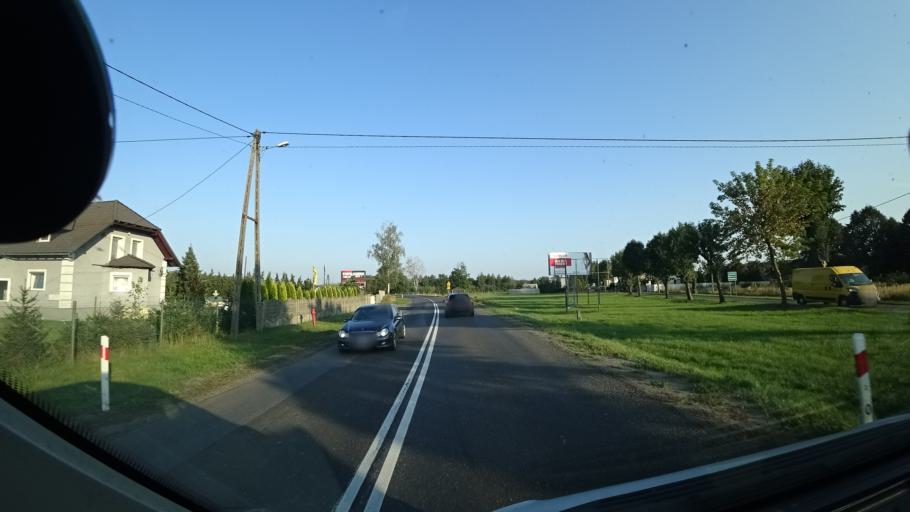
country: PL
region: Opole Voivodeship
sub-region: Powiat kedzierzynsko-kozielski
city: Kedzierzyn-Kozle
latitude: 50.3270
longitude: 18.2023
